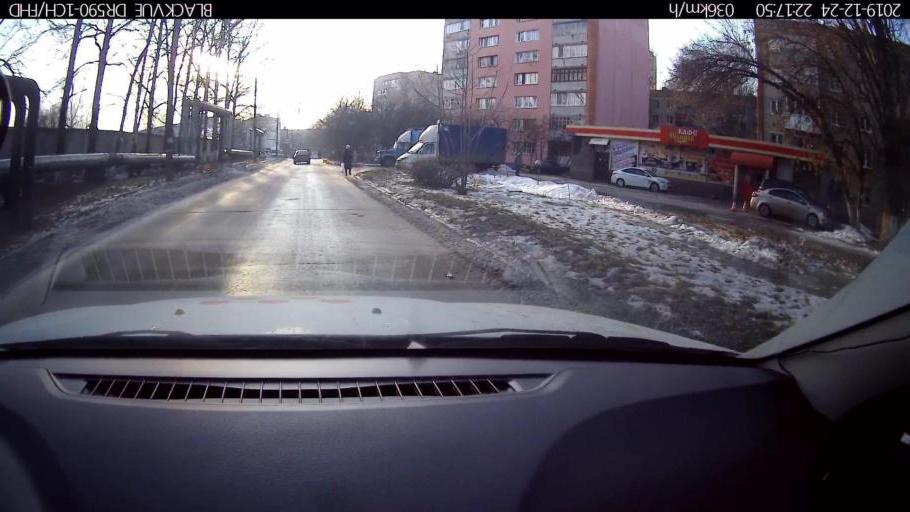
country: RU
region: Nizjnij Novgorod
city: Nizhniy Novgorod
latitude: 56.2401
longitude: 43.9718
